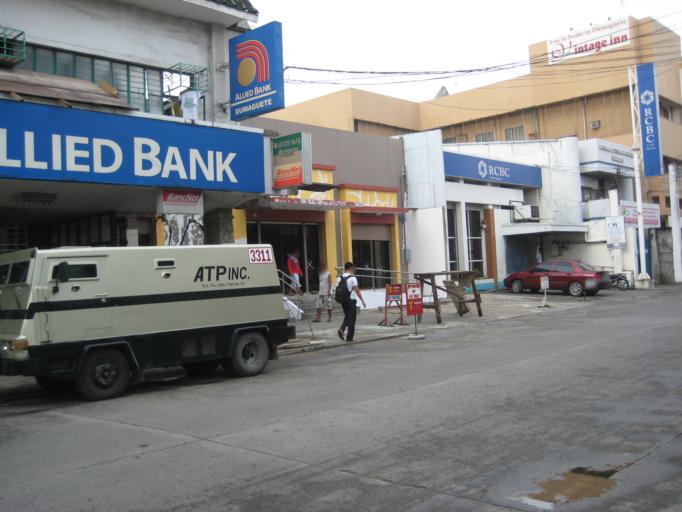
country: PH
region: Central Visayas
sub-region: Province of Negros Oriental
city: Dumaguete
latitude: 9.3069
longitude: 123.3066
